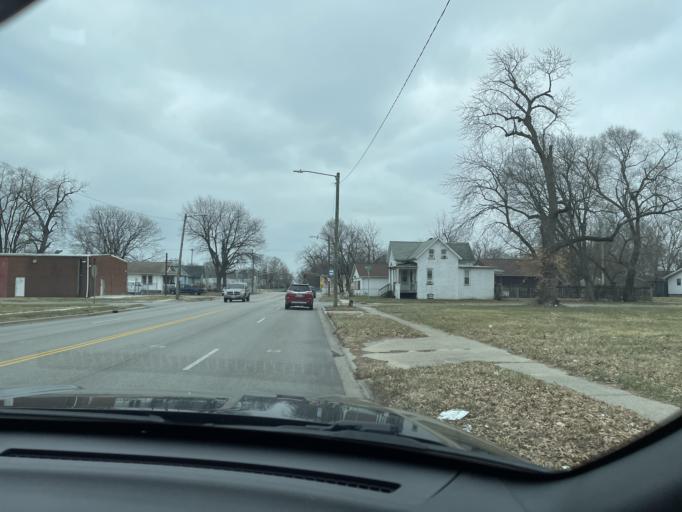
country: US
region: Illinois
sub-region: Sangamon County
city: Springfield
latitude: 39.7946
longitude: -89.6330
